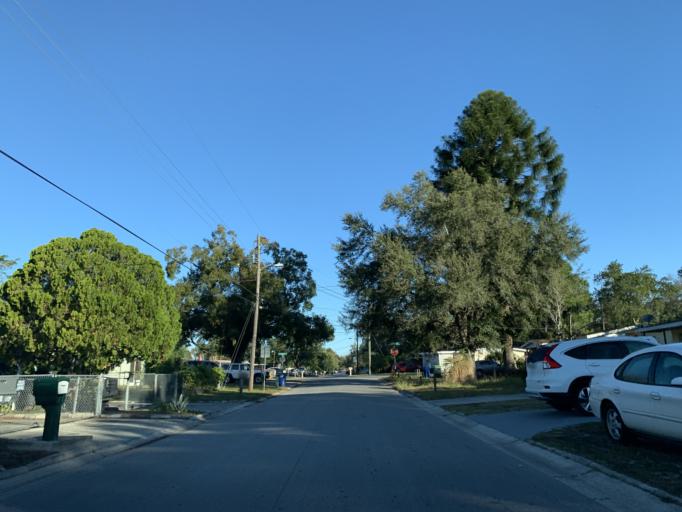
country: US
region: Florida
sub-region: Hillsborough County
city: University
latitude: 28.0430
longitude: -82.4289
